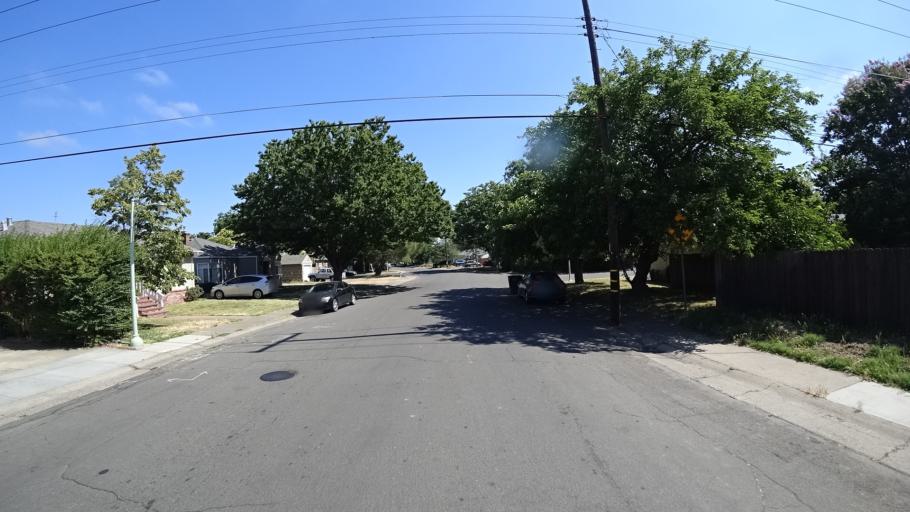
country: US
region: California
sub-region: Sacramento County
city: Parkway
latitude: 38.5337
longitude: -121.4869
